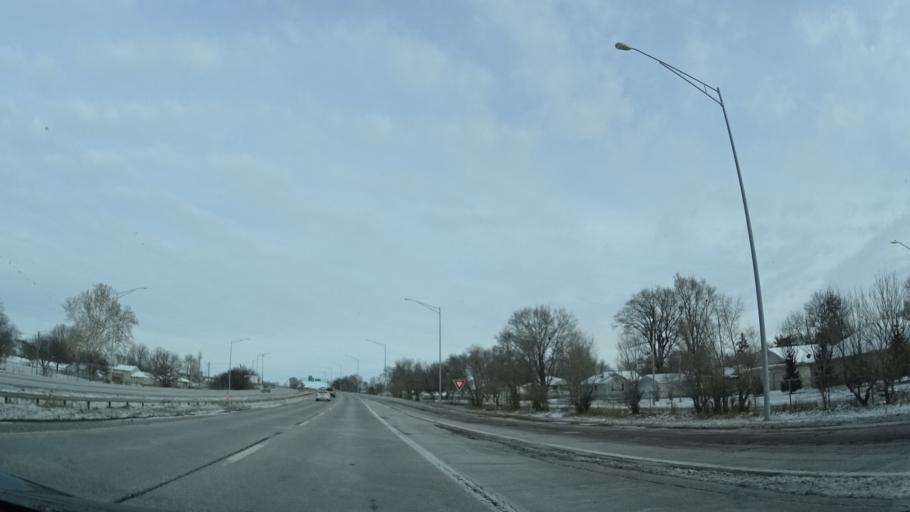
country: US
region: Nebraska
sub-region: Douglas County
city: Omaha
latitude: 41.2561
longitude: -95.9067
